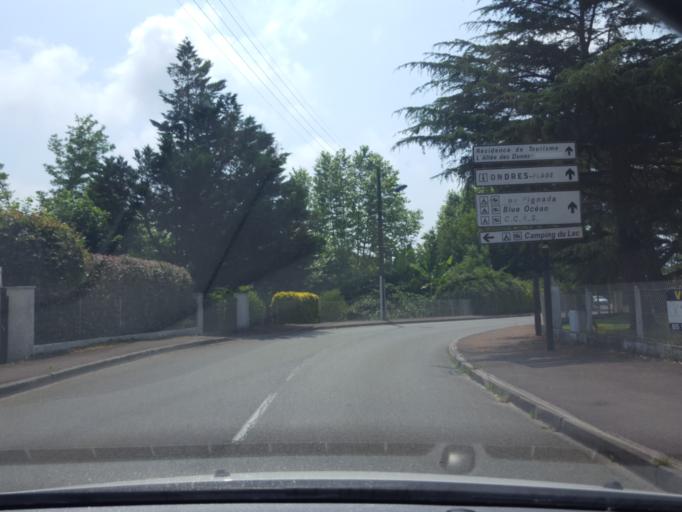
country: FR
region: Aquitaine
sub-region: Departement des Landes
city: Ondres
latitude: 43.5676
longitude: -1.4497
